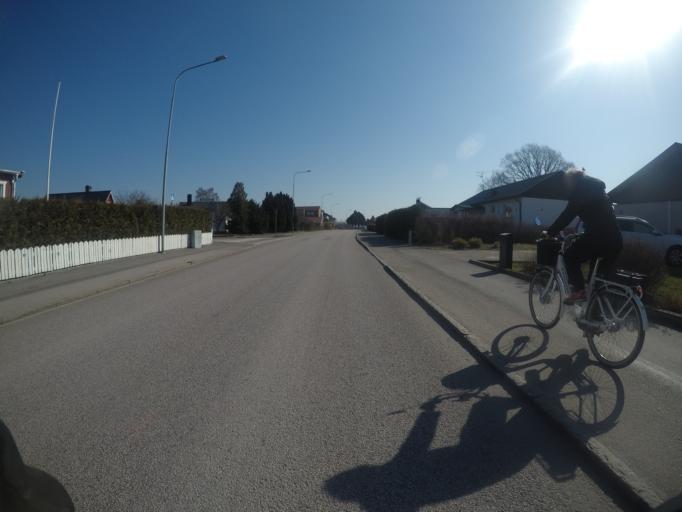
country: SE
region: Halland
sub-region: Laholms Kommun
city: Laholm
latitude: 56.5039
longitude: 13.0431
